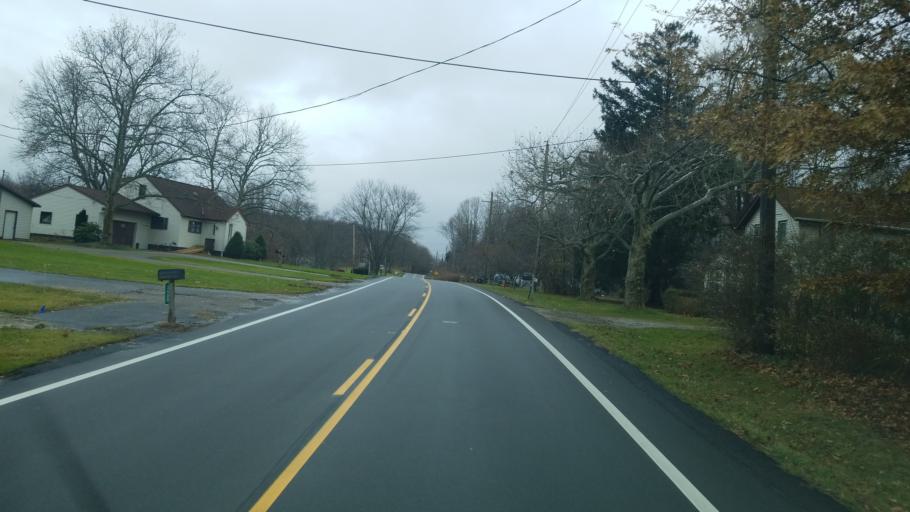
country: US
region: Ohio
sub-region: Ashtabula County
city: Edgewood
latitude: 41.8690
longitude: -80.7478
